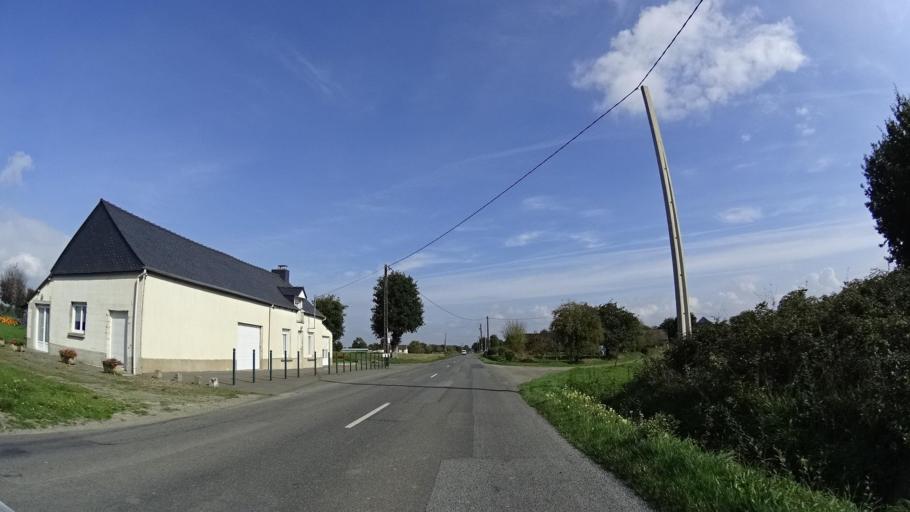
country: FR
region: Brittany
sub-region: Departement d'Ille-et-Vilaine
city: Medreac
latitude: 48.2601
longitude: -2.0972
